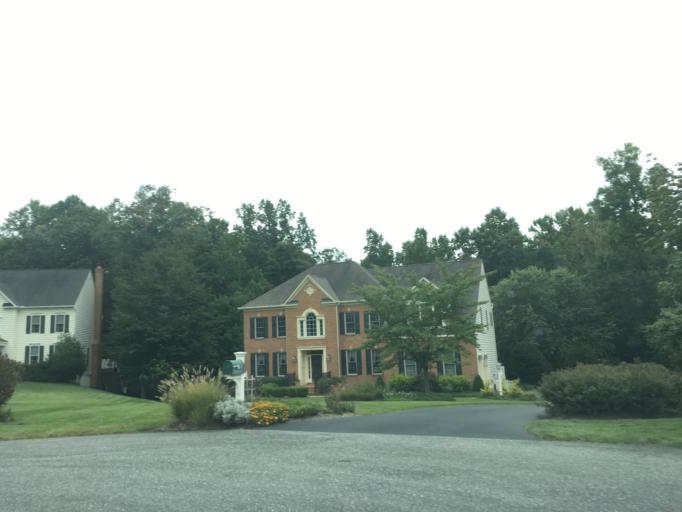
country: US
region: Maryland
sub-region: Anne Arundel County
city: Crownsville
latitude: 39.0330
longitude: -76.5983
